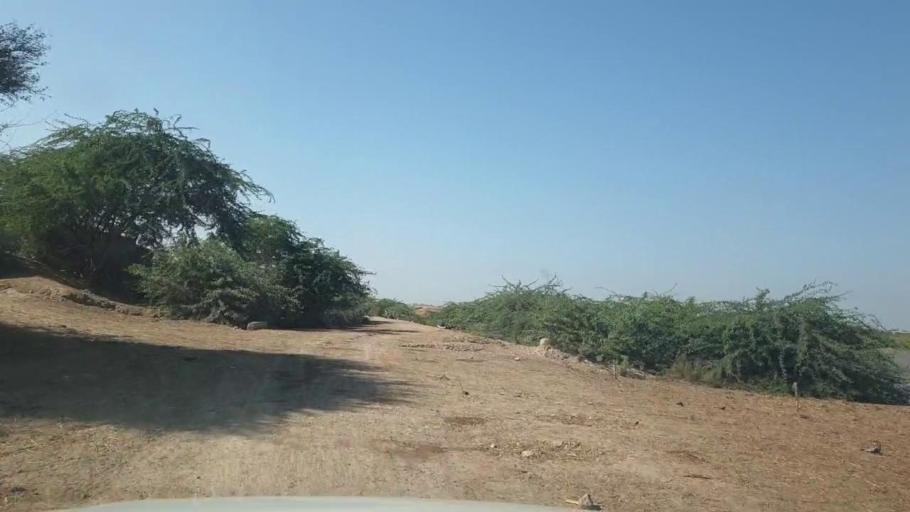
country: PK
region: Sindh
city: Chuhar Jamali
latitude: 24.4394
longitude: 67.8434
